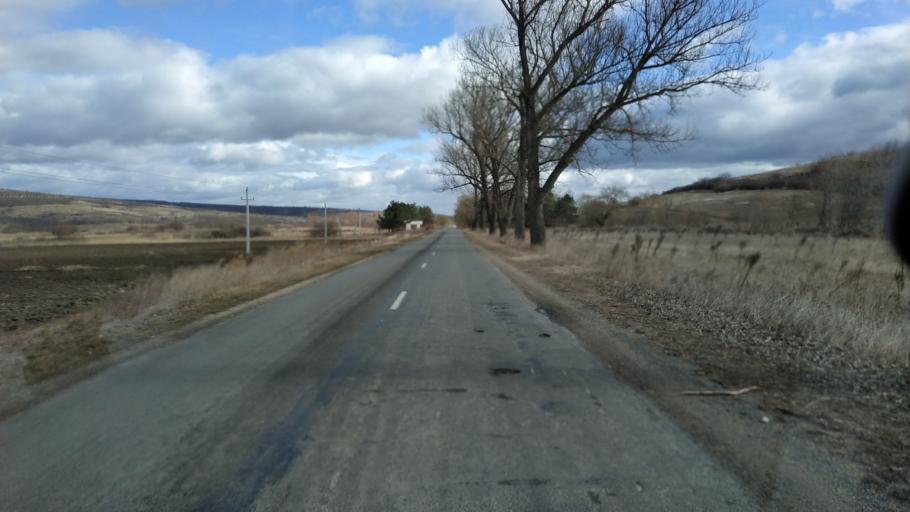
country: MD
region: Calarasi
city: Calarasi
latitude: 47.1409
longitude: 28.3397
